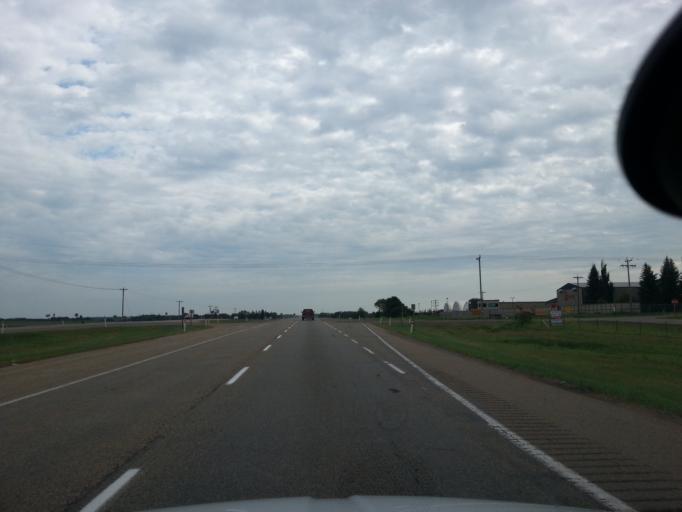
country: CA
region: Alberta
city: Sherwood Park
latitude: 53.5700
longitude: -113.2233
